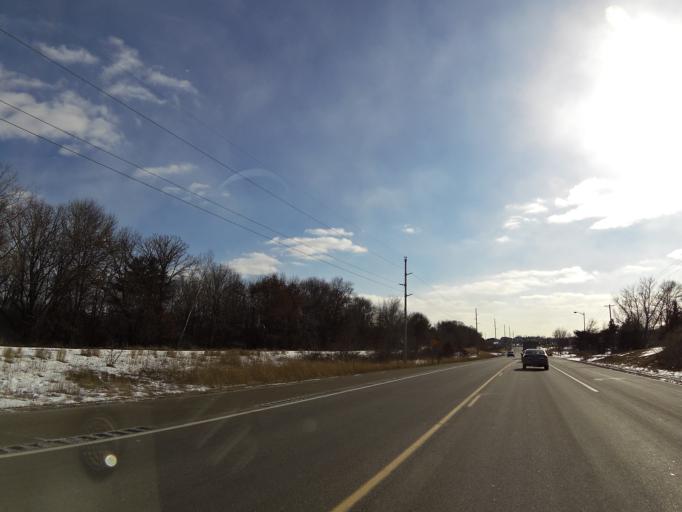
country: US
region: Minnesota
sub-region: Dakota County
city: Rosemount
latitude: 44.7856
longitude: -93.1116
